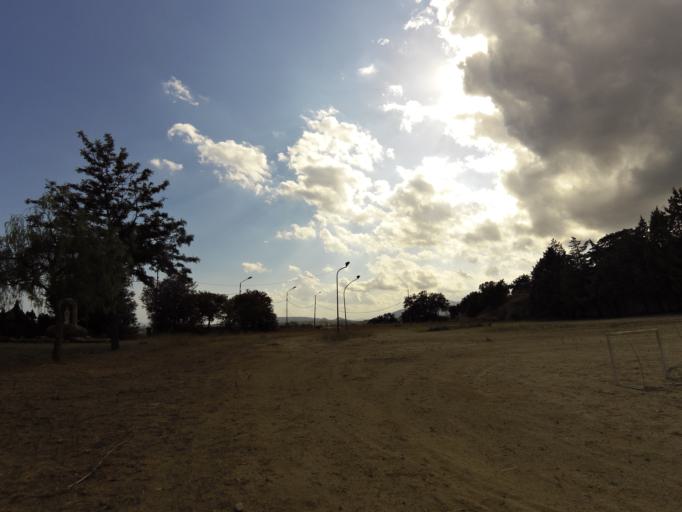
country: IT
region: Calabria
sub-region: Provincia di Reggio Calabria
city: Riace
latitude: 38.4107
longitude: 16.4836
